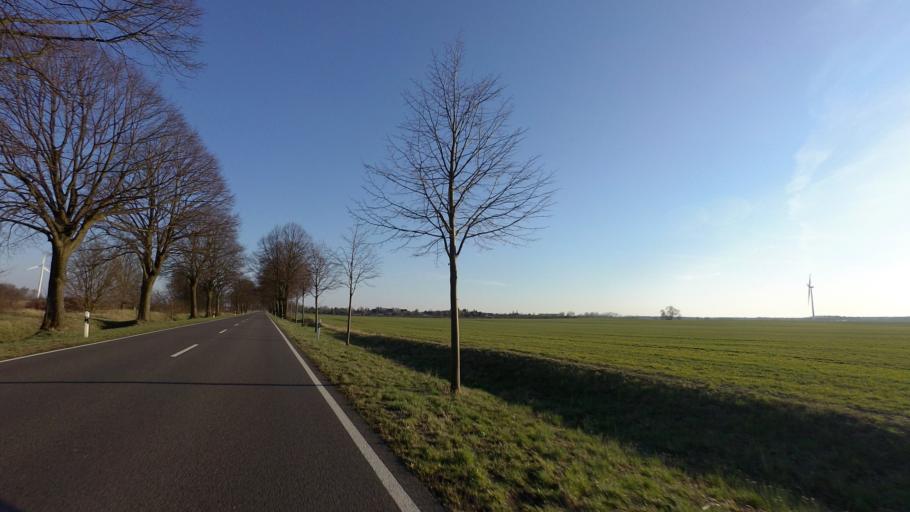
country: DE
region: Brandenburg
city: Eberswalde
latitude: 52.7514
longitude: 13.8433
